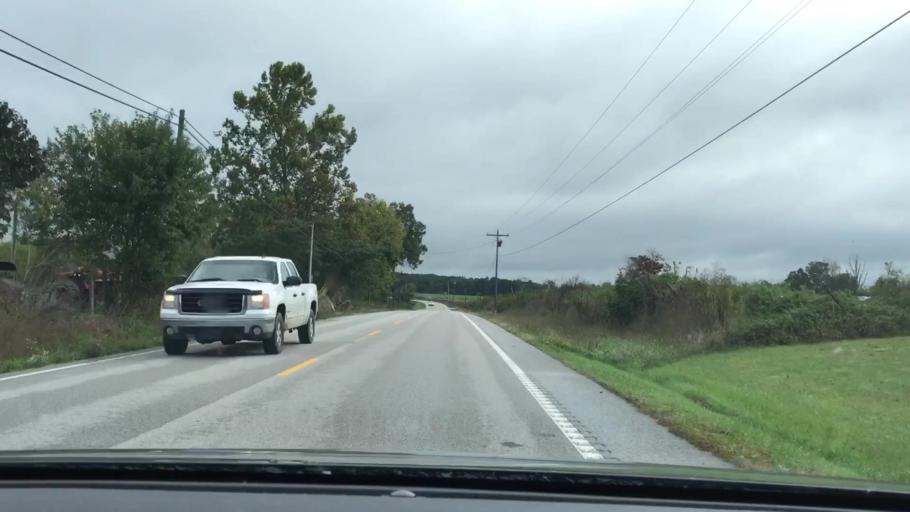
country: US
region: Tennessee
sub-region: Fentress County
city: Jamestown
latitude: 36.3642
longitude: -84.8097
